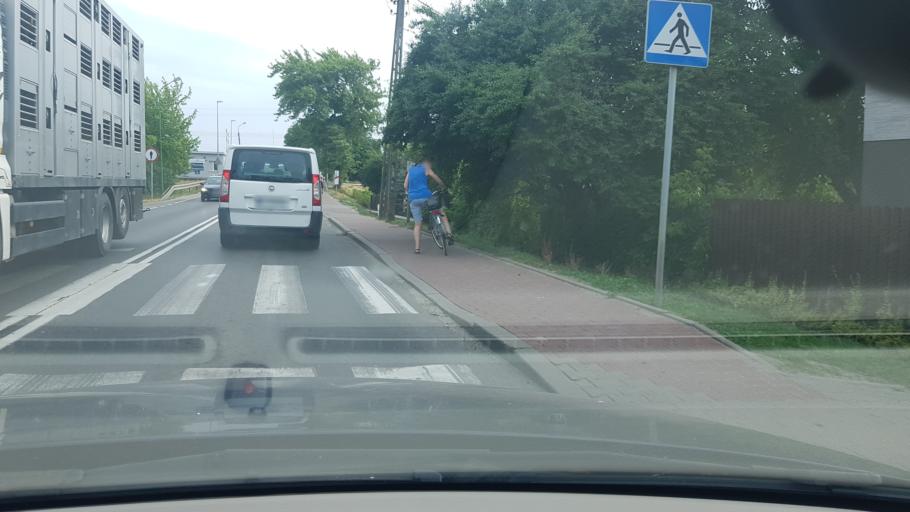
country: PL
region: Lodz Voivodeship
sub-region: Powiat tomaszowski
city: Tomaszow Mazowiecki
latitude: 51.5554
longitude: 20.0184
